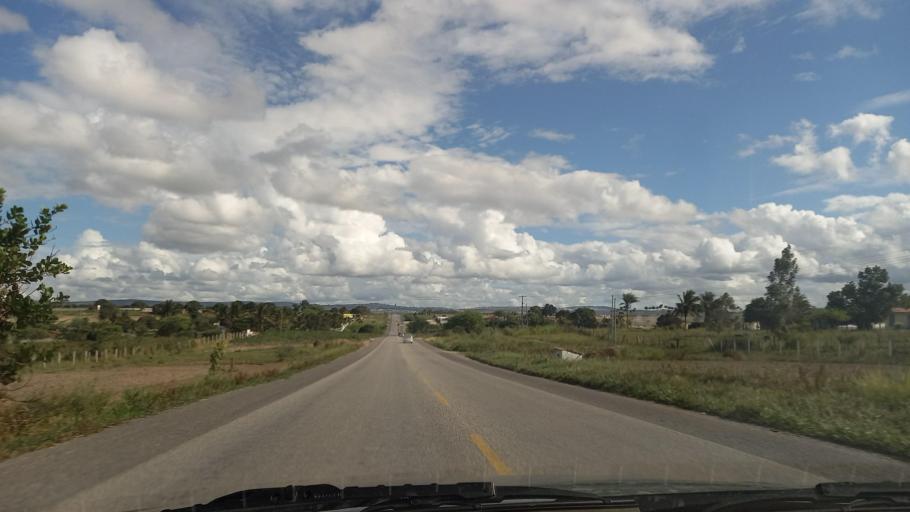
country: BR
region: Pernambuco
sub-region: Sao Joao
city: Sao Joao
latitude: -8.7801
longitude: -36.4300
